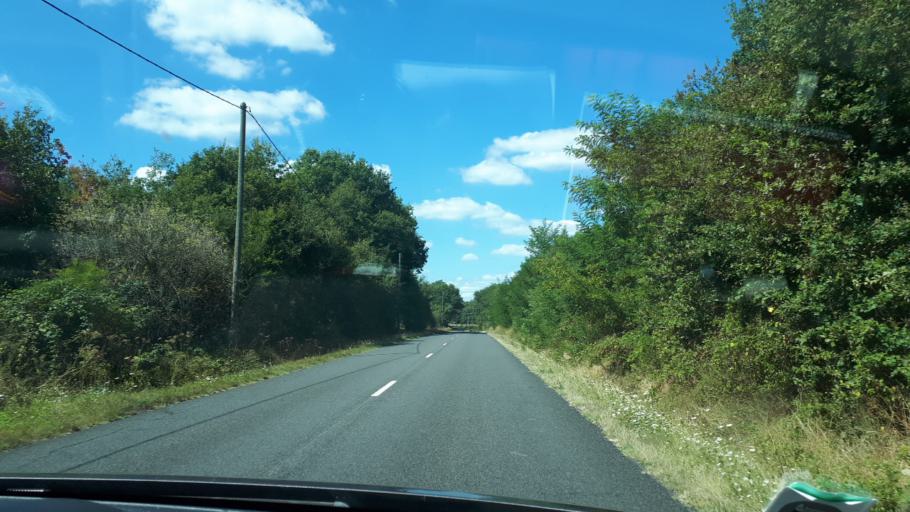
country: FR
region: Centre
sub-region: Departement du Loir-et-Cher
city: Neung-sur-Beuvron
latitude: 47.5344
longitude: 1.7562
